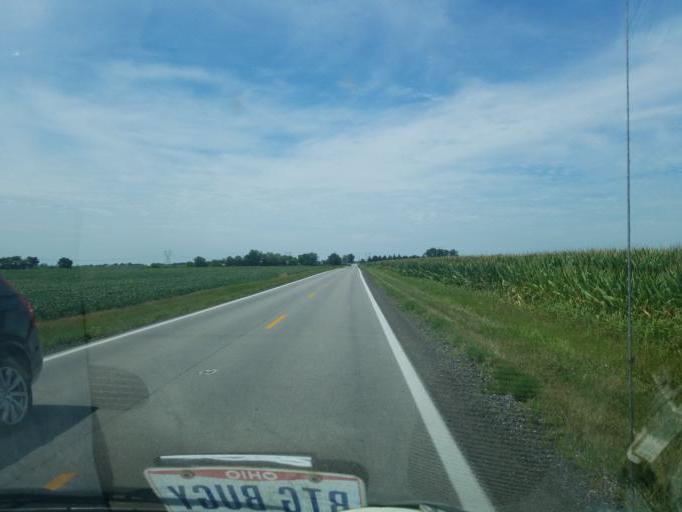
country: US
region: Ohio
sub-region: Madison County
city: West Jefferson
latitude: 39.8697
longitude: -83.2853
